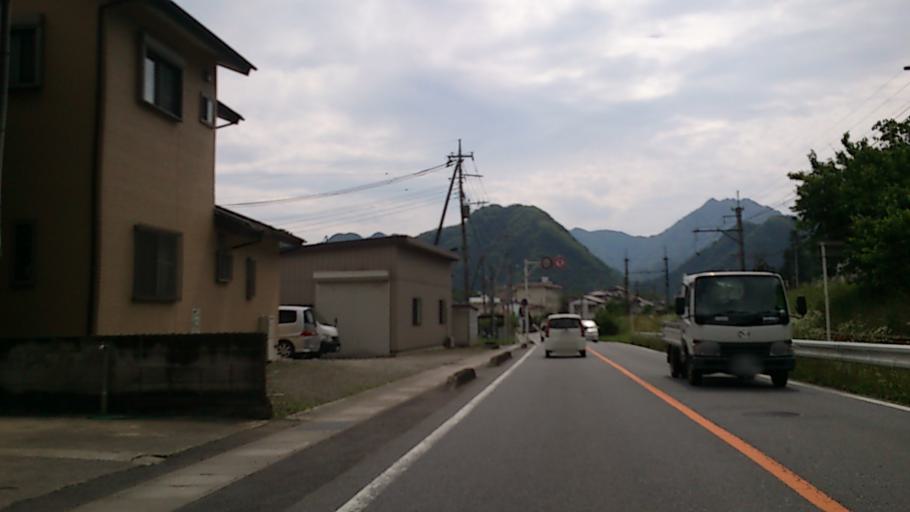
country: JP
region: Gunma
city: Tomioka
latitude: 36.2117
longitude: 138.7969
